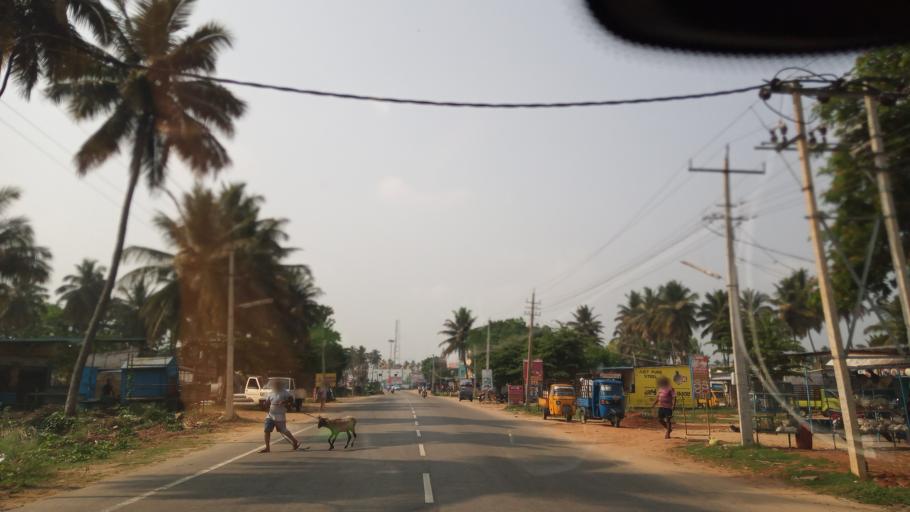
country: IN
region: Karnataka
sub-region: Mandya
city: Pandavapura
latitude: 12.5084
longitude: 76.6747
